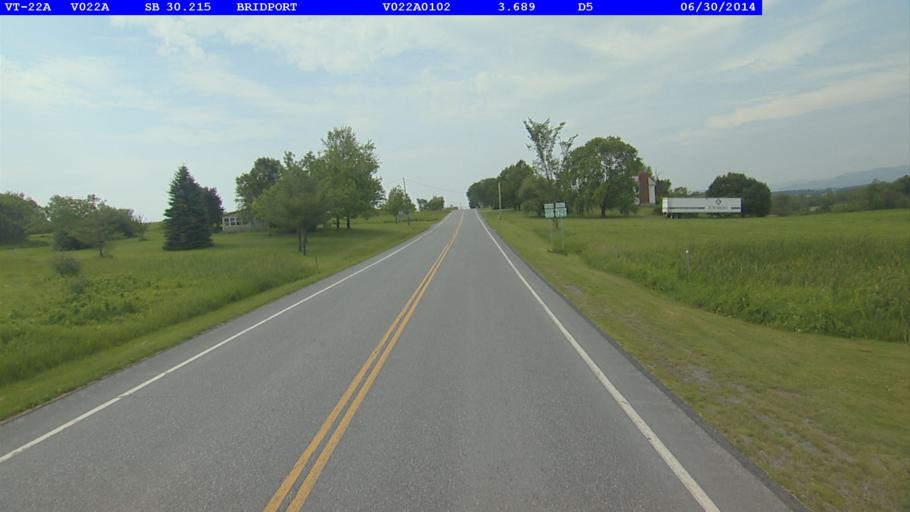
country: US
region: Vermont
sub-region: Addison County
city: Middlebury (village)
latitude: 43.9933
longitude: -73.3118
